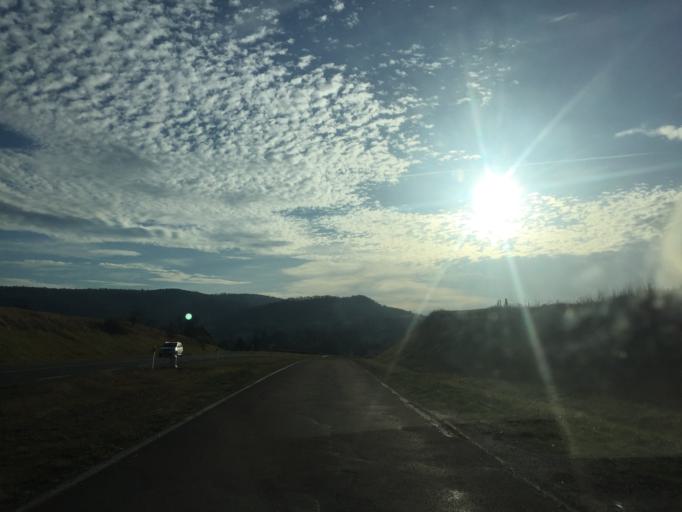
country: FR
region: Franche-Comte
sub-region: Departement du Jura
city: Arbois
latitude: 46.9161
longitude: 5.7711
